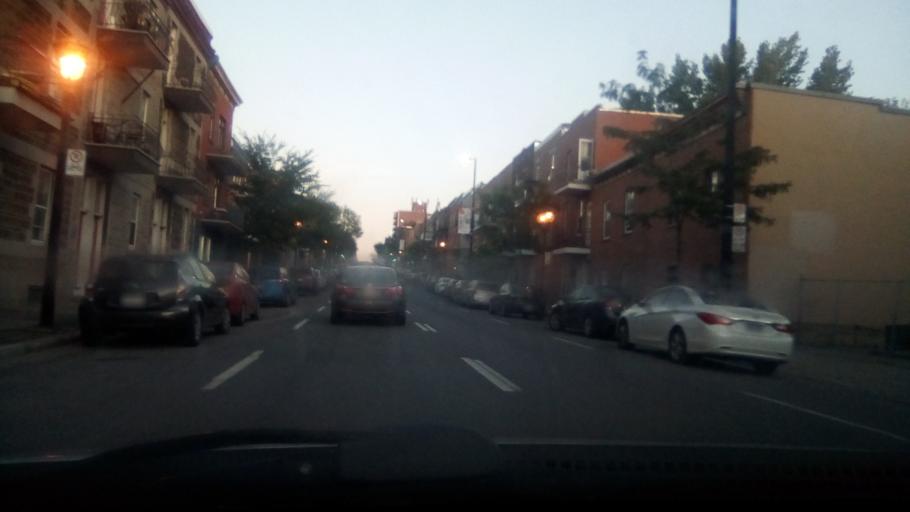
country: CA
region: Quebec
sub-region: Monteregie
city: Longueuil
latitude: 45.5347
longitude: -73.5567
